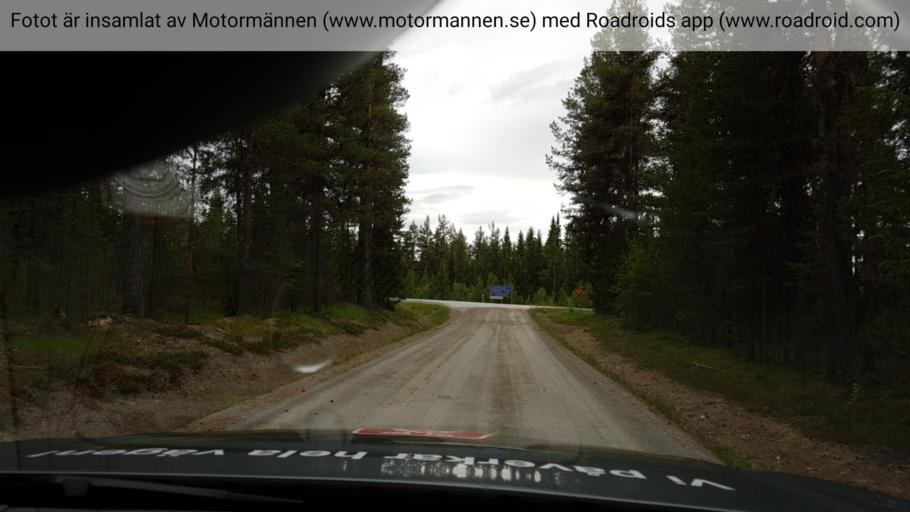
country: SE
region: Jaemtland
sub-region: Bergs Kommun
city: Hoverberg
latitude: 62.7571
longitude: 13.8207
